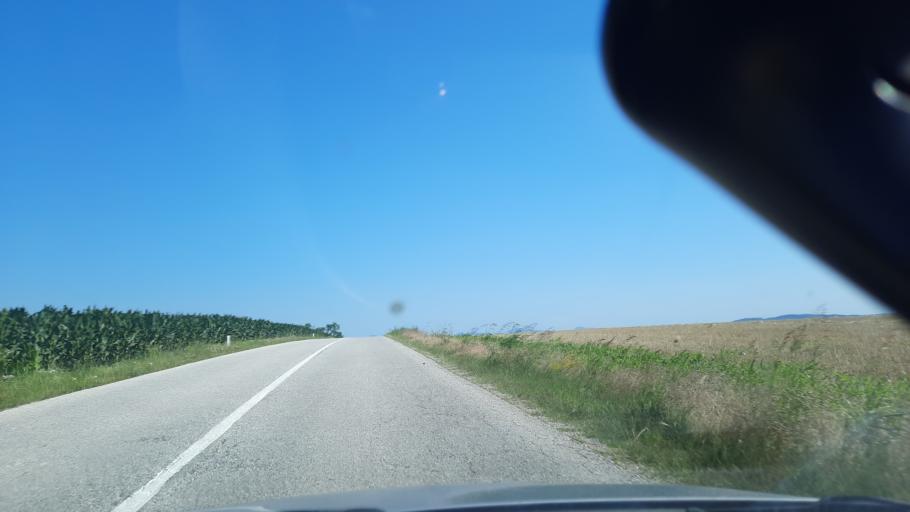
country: RS
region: Central Serbia
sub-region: Branicevski Okrug
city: Malo Crnice
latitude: 44.5778
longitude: 21.4202
